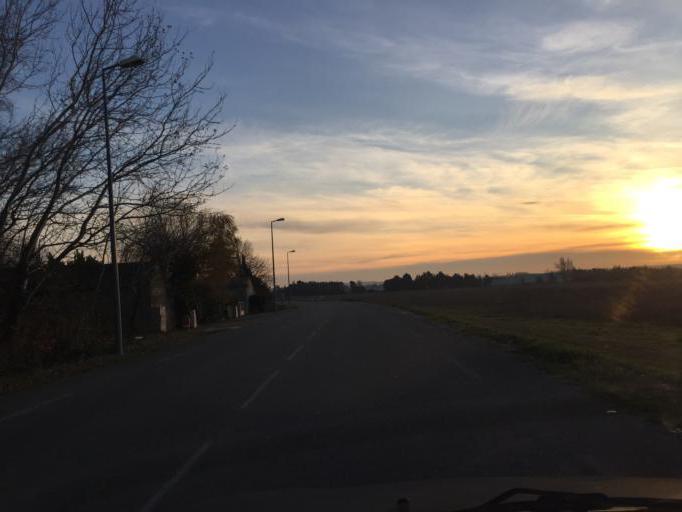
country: FR
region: Provence-Alpes-Cote d'Azur
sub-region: Departement du Vaucluse
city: Jonquieres
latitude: 44.1091
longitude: 4.8938
